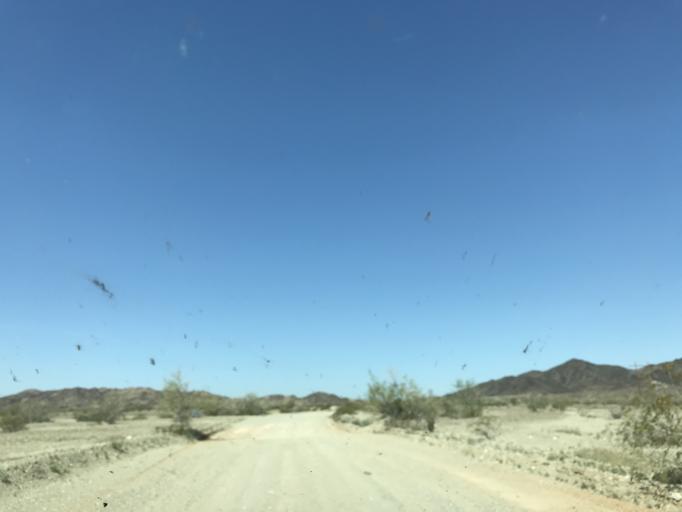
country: US
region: California
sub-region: Riverside County
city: Mesa Verde
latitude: 33.4918
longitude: -114.8074
